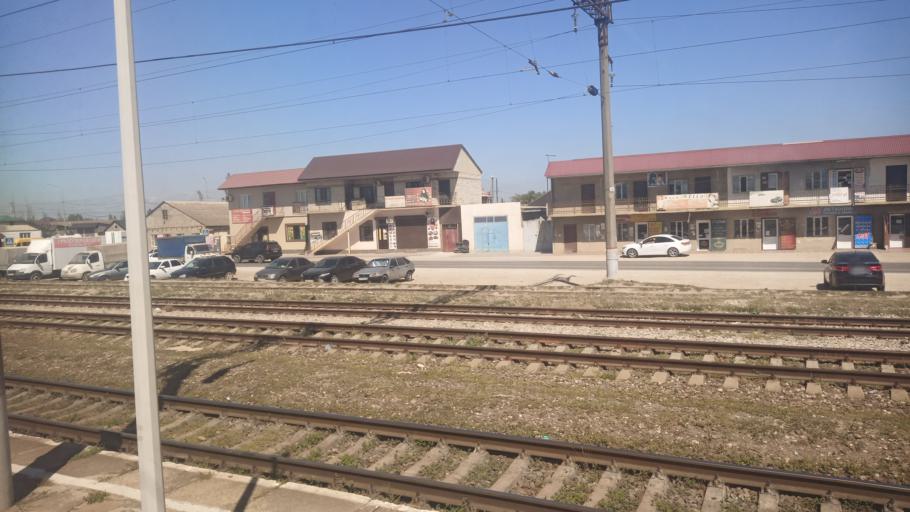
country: RU
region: Dagestan
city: Shamkhal
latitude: 43.0533
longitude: 47.3328
